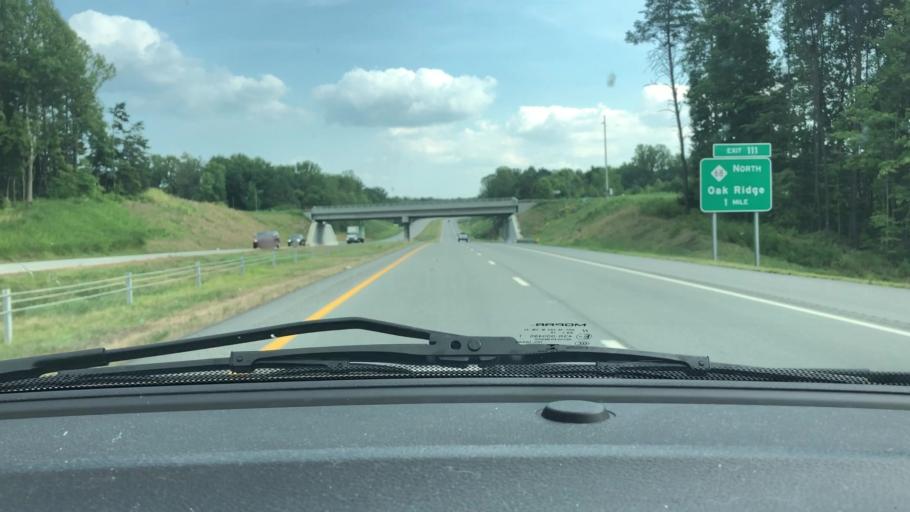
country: US
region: North Carolina
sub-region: Guilford County
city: Oak Ridge
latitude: 36.1543
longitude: -79.9595
